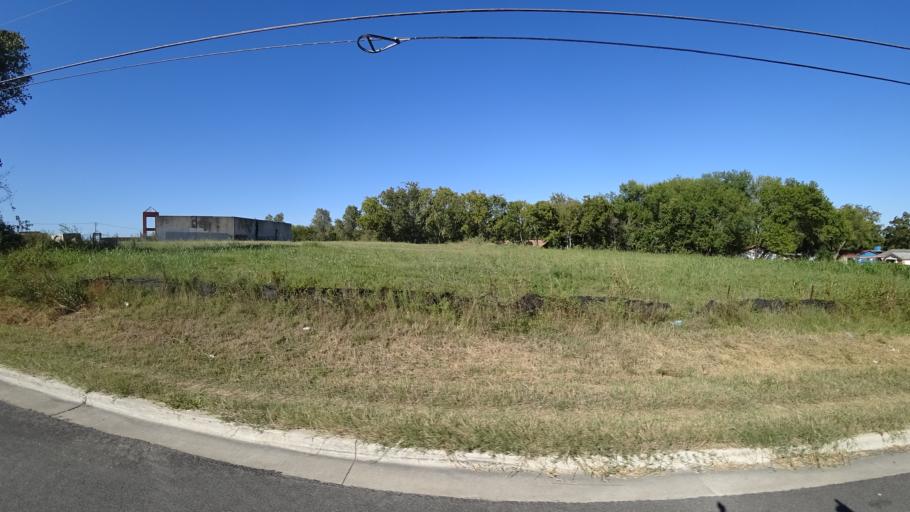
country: US
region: Texas
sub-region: Travis County
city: Austin
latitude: 30.2852
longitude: -97.6624
